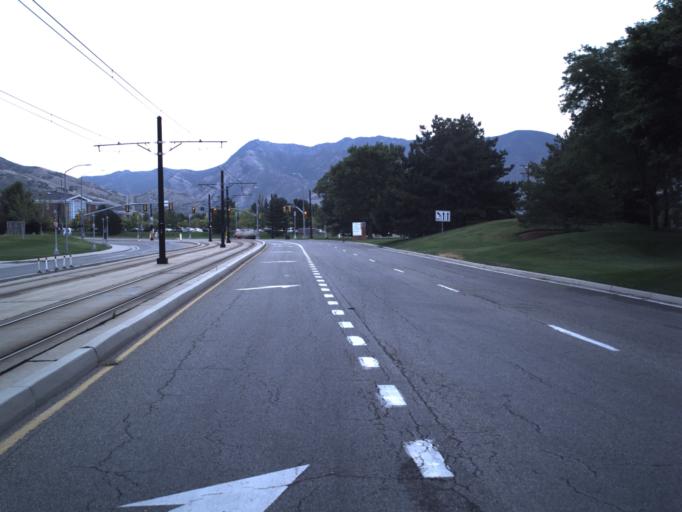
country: US
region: Utah
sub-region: Salt Lake County
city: Salt Lake City
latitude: 40.7595
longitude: -111.8440
